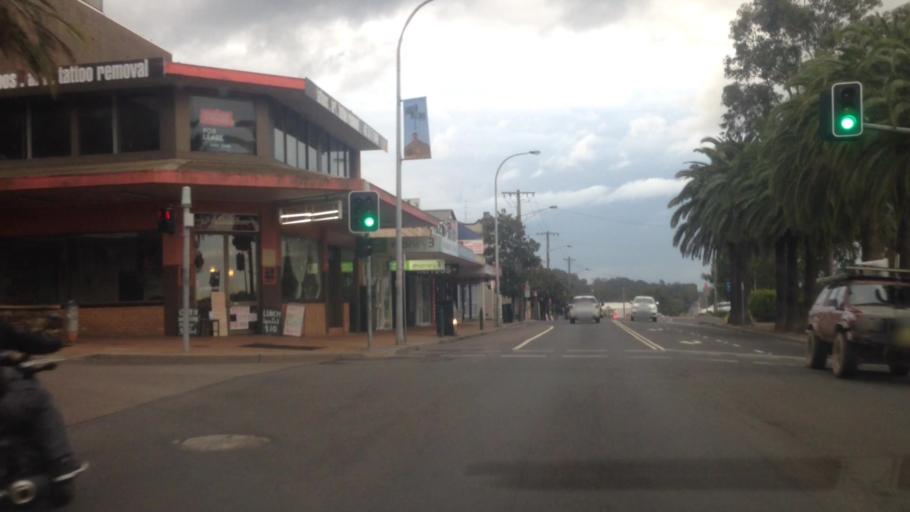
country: AU
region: New South Wales
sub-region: Wyong Shire
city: Chittaway Bay
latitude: -33.2844
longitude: 151.4249
